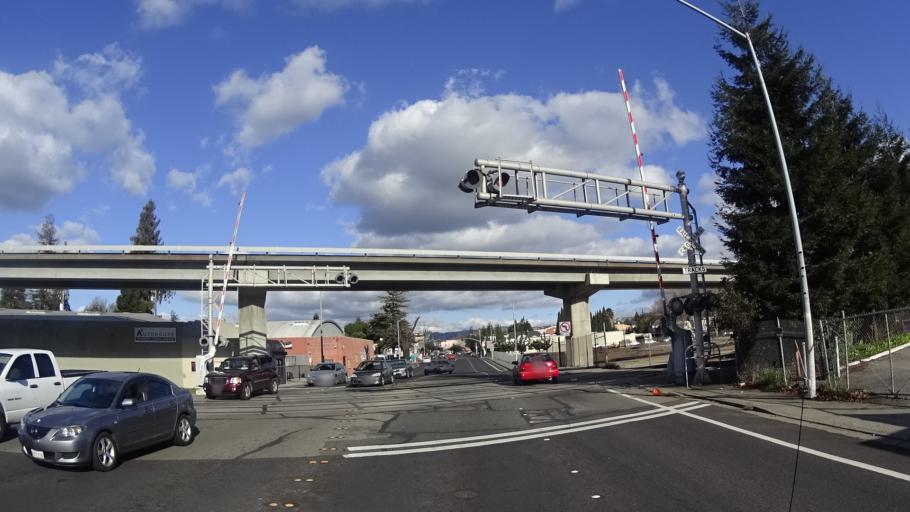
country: US
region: California
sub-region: Alameda County
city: Hayward
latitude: 37.6710
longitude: -122.0896
